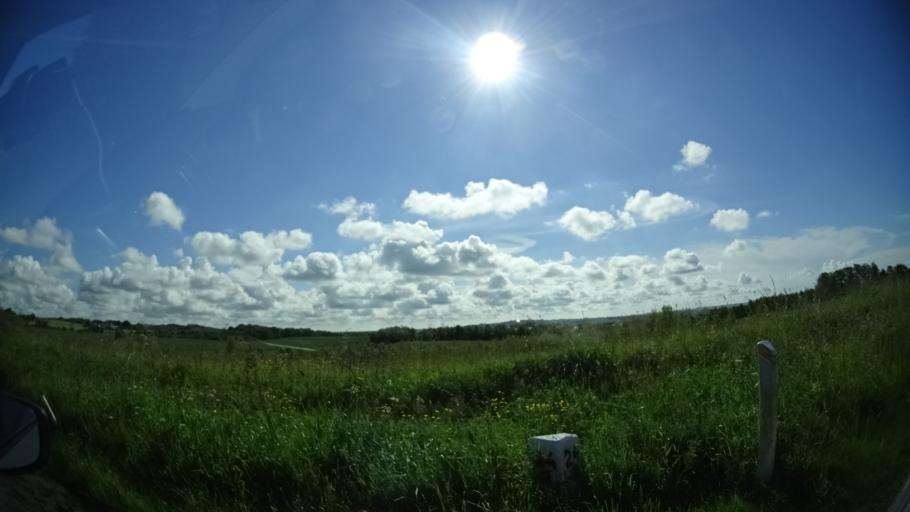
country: DK
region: Central Jutland
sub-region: Syddjurs Kommune
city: Ronde
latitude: 56.3105
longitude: 10.4167
